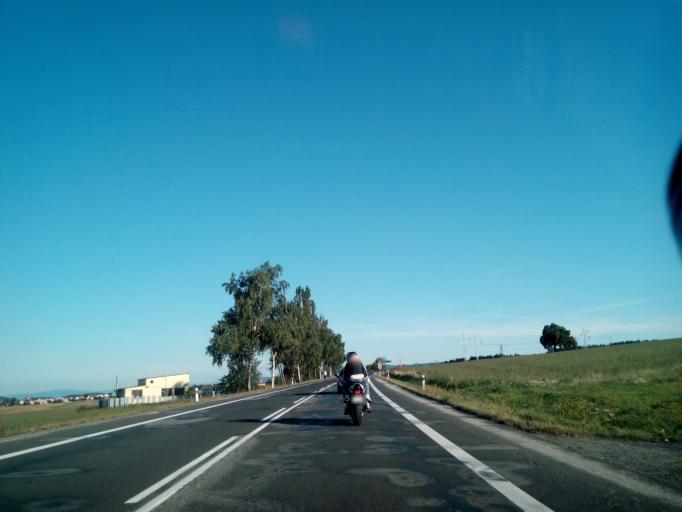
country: SK
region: Presovsky
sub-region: Okres Poprad
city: Poprad
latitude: 49.0421
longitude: 20.3277
